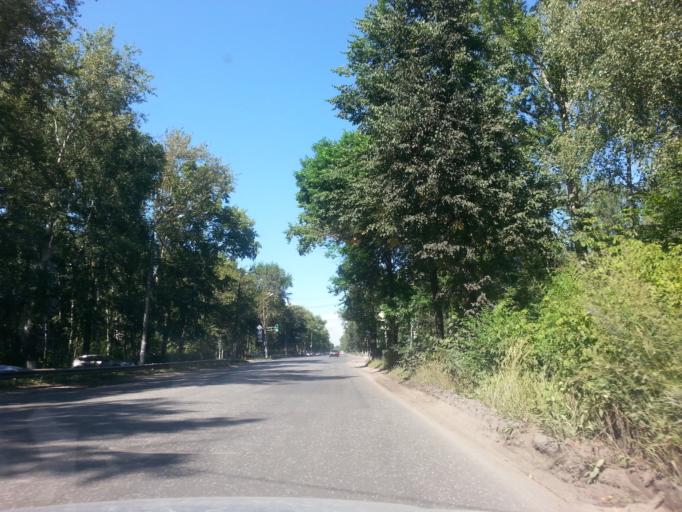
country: RU
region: Nizjnij Novgorod
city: Gorbatovka
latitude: 56.3384
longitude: 43.8457
